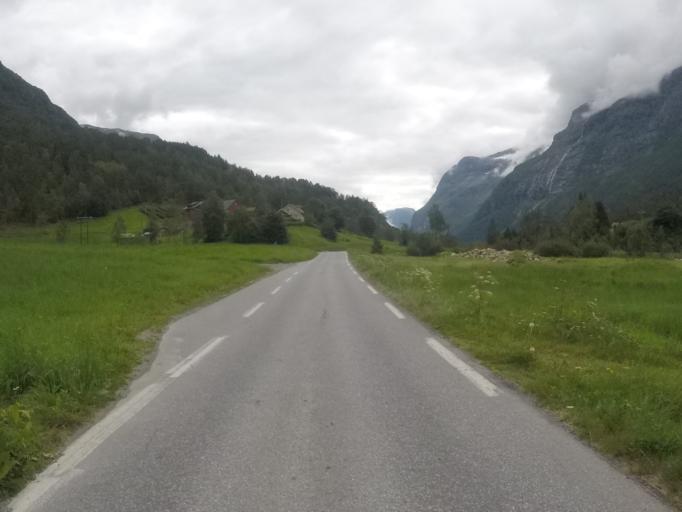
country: NO
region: Sogn og Fjordane
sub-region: Stryn
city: Stryn
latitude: 61.8659
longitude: 6.8832
